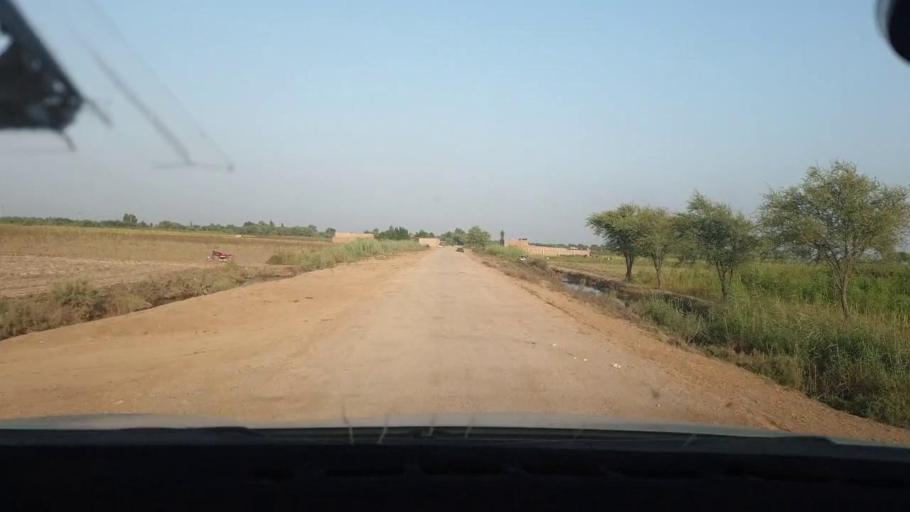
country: PK
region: Sindh
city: Shahdadpur
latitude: 25.8943
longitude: 68.6725
